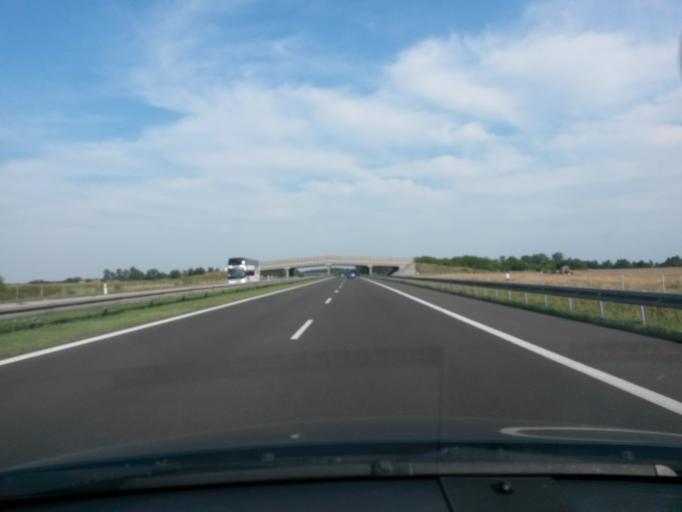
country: PL
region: Greater Poland Voivodeship
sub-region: Powiat slupecki
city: Strzalkowo
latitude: 52.2689
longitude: 17.7266
